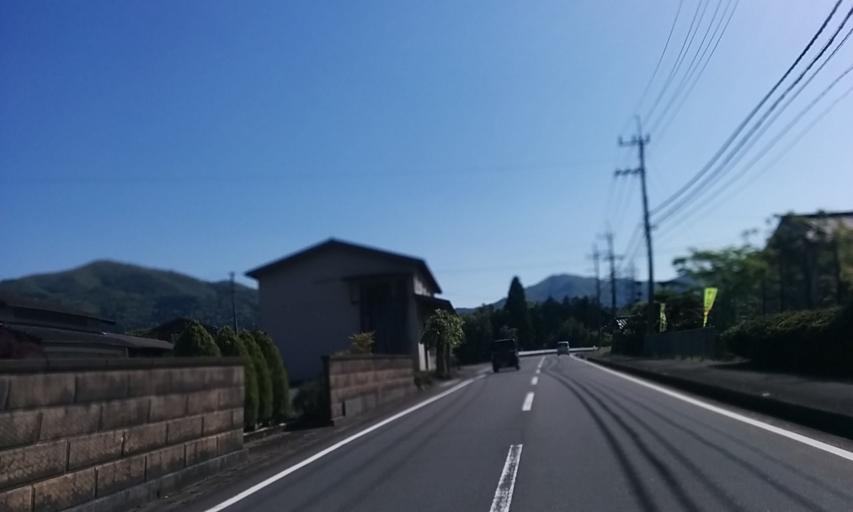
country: JP
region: Kyoto
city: Ayabe
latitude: 35.2563
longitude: 135.4253
